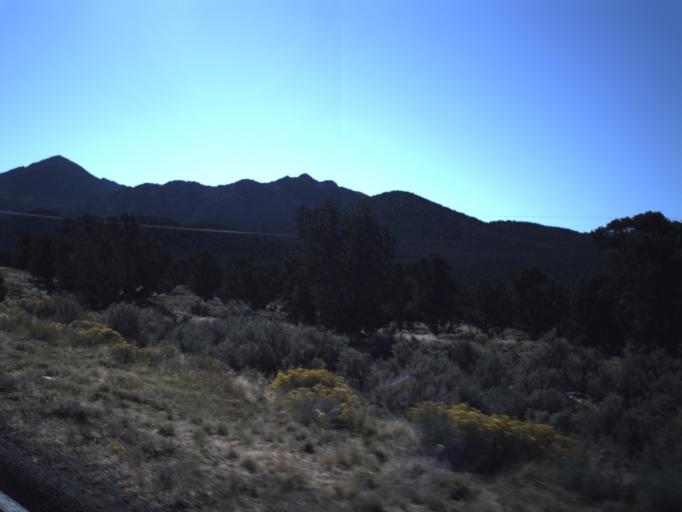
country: US
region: Utah
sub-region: Washington County
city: Enterprise
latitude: 37.6121
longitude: -113.4020
